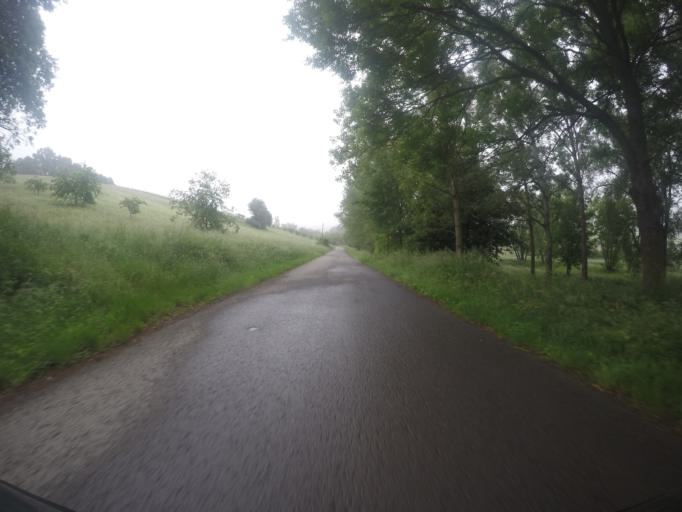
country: DE
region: Bavaria
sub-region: Regierungsbezirk Unterfranken
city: Schwanfeld
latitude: 49.9187
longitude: 10.1506
